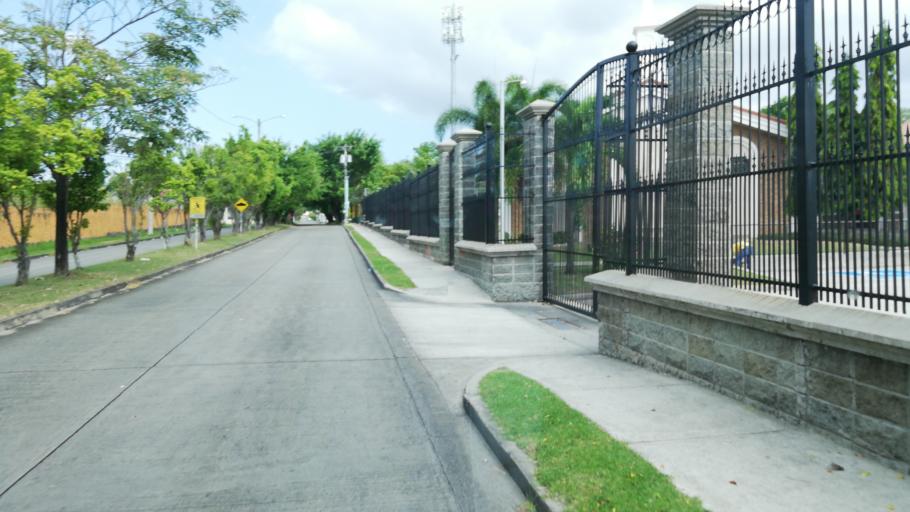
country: PA
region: Panama
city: San Miguelito
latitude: 9.0570
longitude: -79.4597
